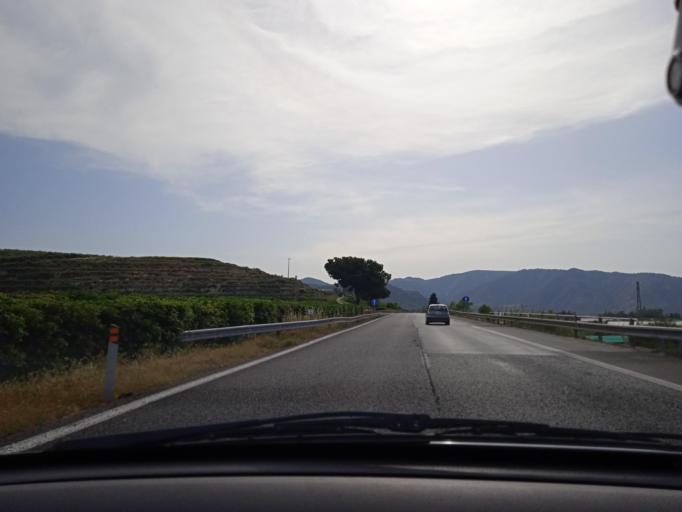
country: IT
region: Sicily
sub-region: Messina
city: Tonnarella
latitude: 38.1146
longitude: 15.1019
